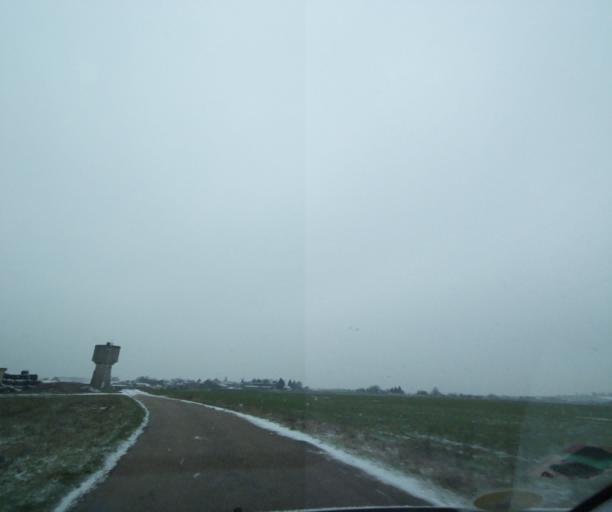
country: FR
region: Champagne-Ardenne
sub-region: Departement de la Haute-Marne
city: Wassy
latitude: 48.4676
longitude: 4.9998
